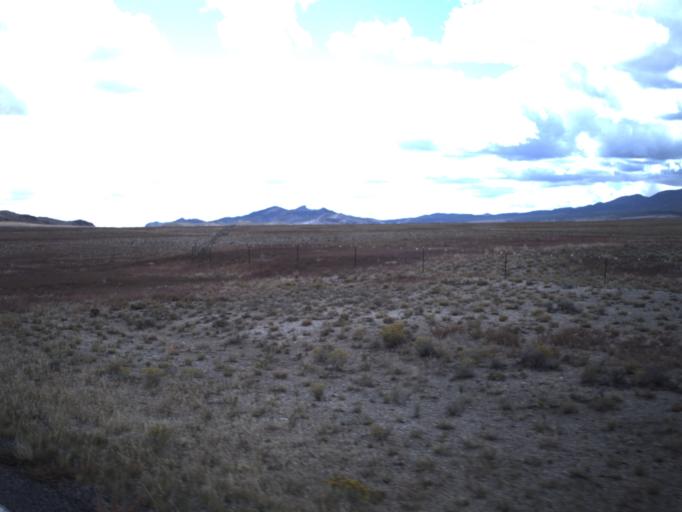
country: US
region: Utah
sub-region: Beaver County
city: Milford
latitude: 38.6379
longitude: -113.8595
